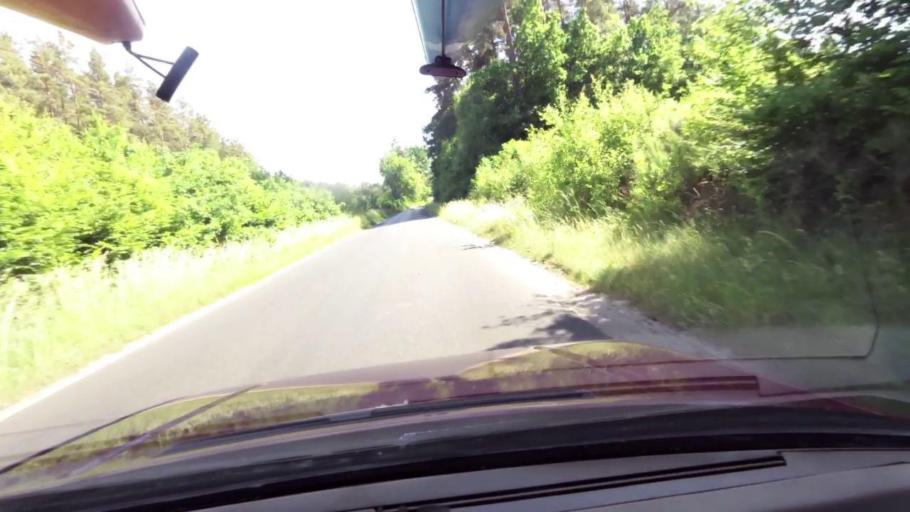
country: PL
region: Pomeranian Voivodeship
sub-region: Powiat slupski
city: Kepice
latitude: 54.2115
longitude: 16.8947
